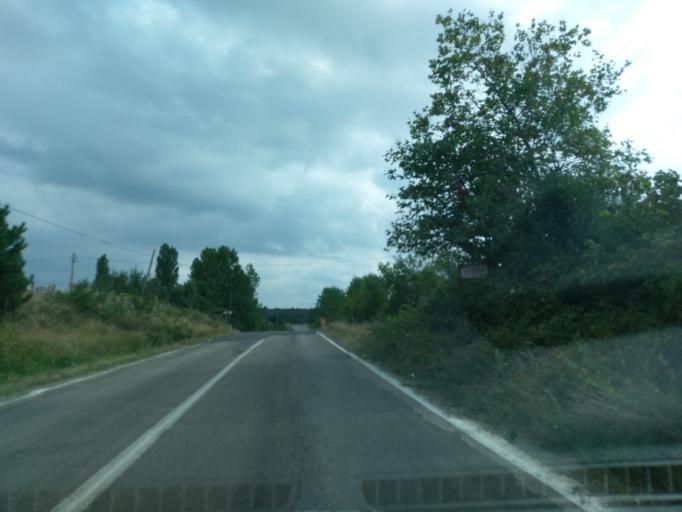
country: TR
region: Sinop
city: Yenikonak
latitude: 41.9423
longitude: 34.7249
